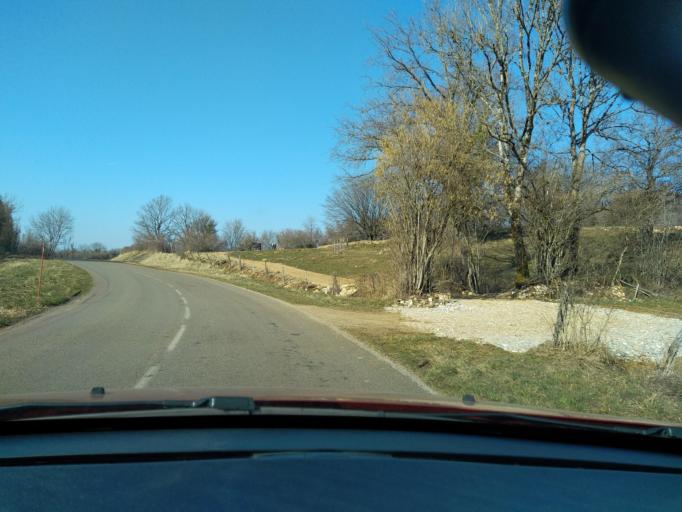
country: FR
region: Franche-Comte
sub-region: Departement du Jura
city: Perrigny
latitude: 46.6216
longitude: 5.6411
